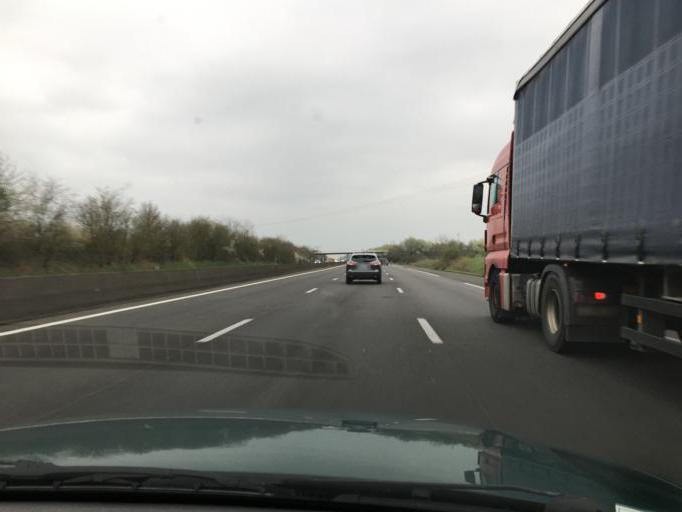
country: FR
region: Centre
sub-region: Departement du Loiret
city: Ingre
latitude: 47.9005
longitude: 1.8137
